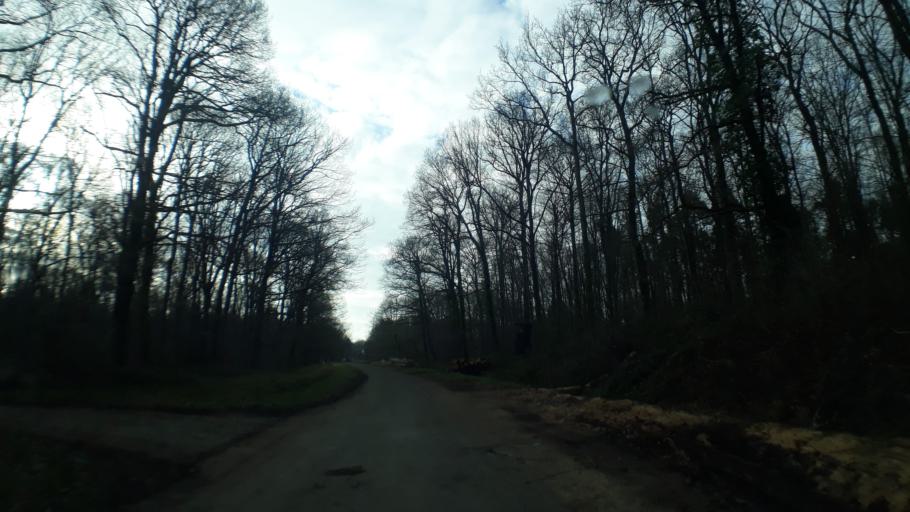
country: DE
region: North Rhine-Westphalia
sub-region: Regierungsbezirk Koln
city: Euskirchen
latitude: 50.6287
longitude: 6.7618
